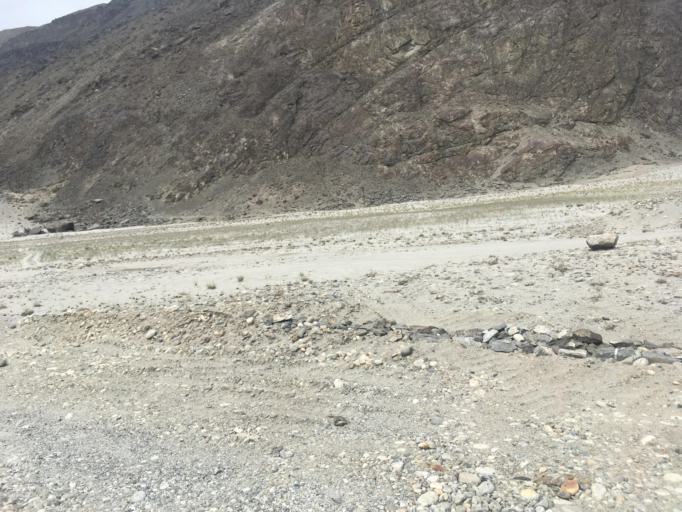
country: PK
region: Gilgit-Baltistan
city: Skardu
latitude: 35.3143
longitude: 75.6576
